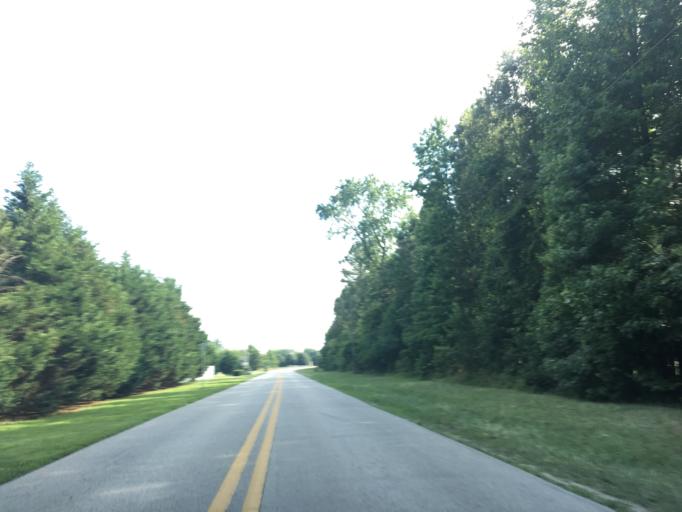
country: US
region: Delaware
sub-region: Sussex County
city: Bridgeville
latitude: 38.7630
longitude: -75.4957
